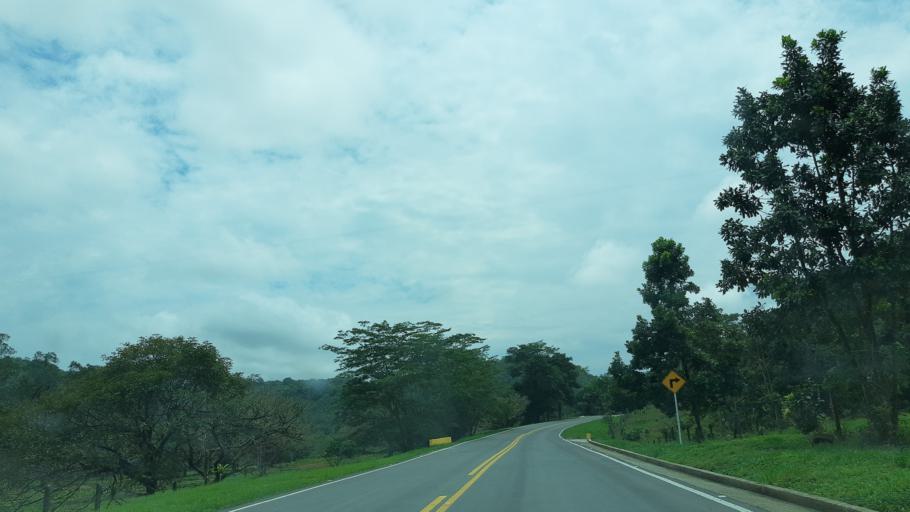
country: CO
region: Boyaca
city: San Luis de Gaceno
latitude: 4.8293
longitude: -73.1461
